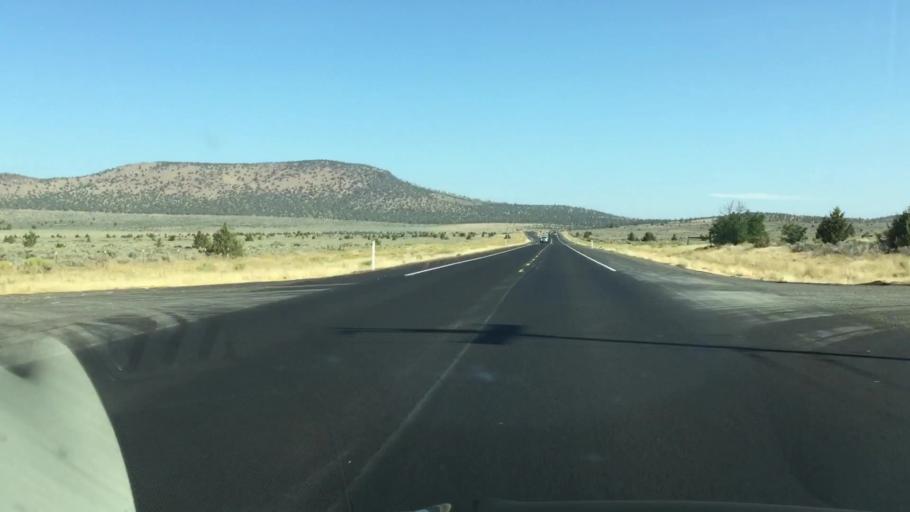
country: US
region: Oregon
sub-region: Jefferson County
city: Culver
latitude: 44.4481
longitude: -121.1995
